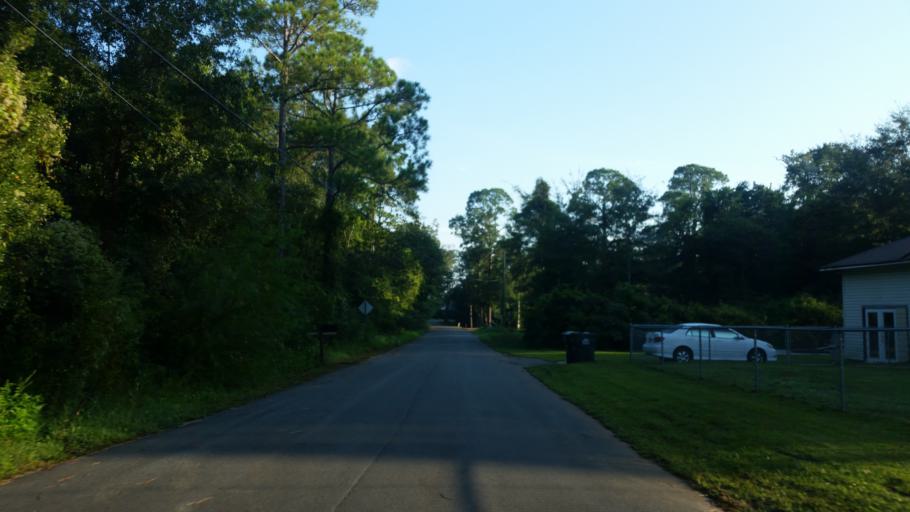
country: US
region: Florida
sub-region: Santa Rosa County
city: East Milton
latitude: 30.6285
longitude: -87.0193
